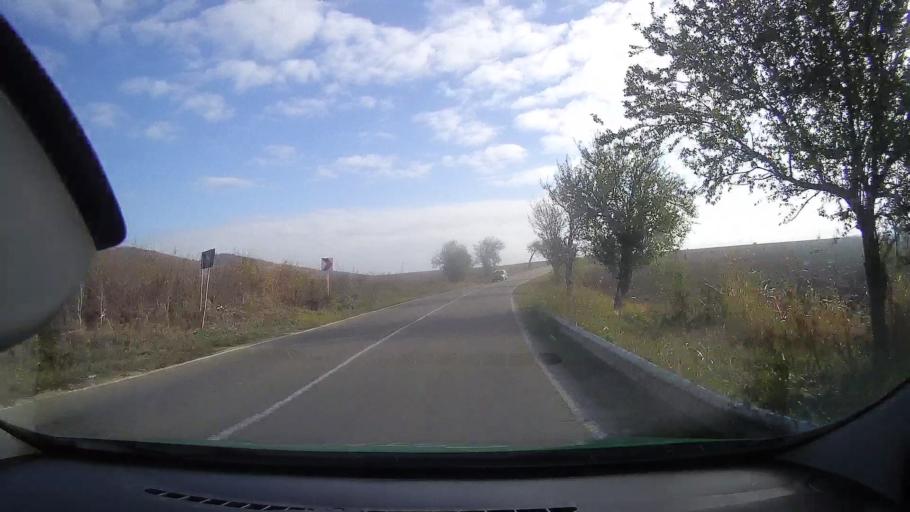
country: RO
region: Tulcea
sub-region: Comuna Bestepe
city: Bestepe
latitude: 45.0820
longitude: 29.0295
